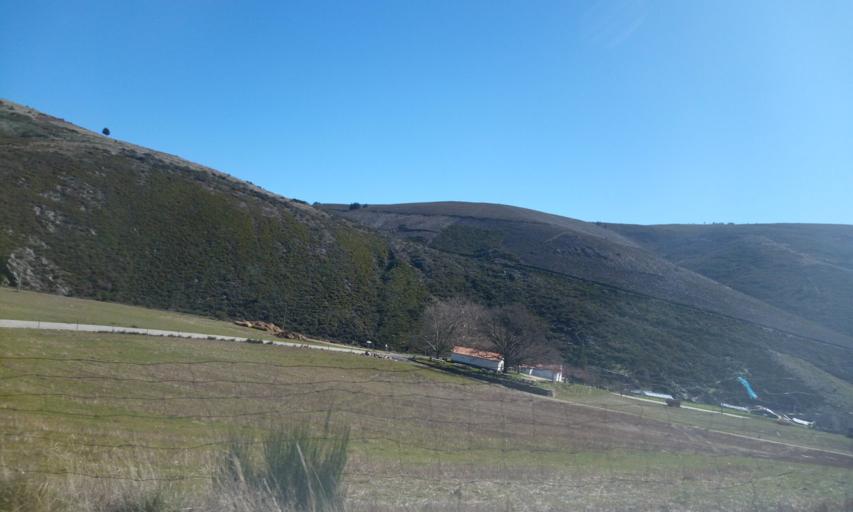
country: PT
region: Guarda
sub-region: Manteigas
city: Manteigas
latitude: 40.4576
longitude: -7.4932
